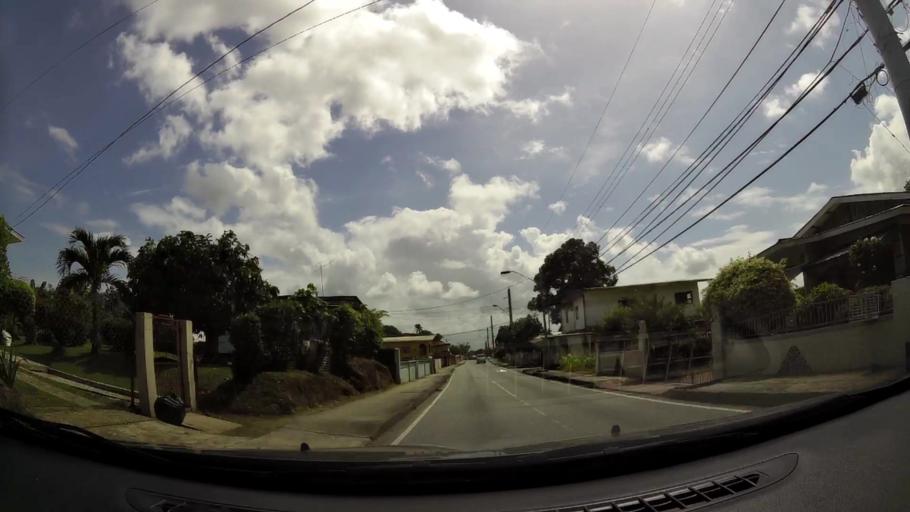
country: TT
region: Borough of Arima
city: Arima
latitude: 10.6355
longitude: -61.2763
